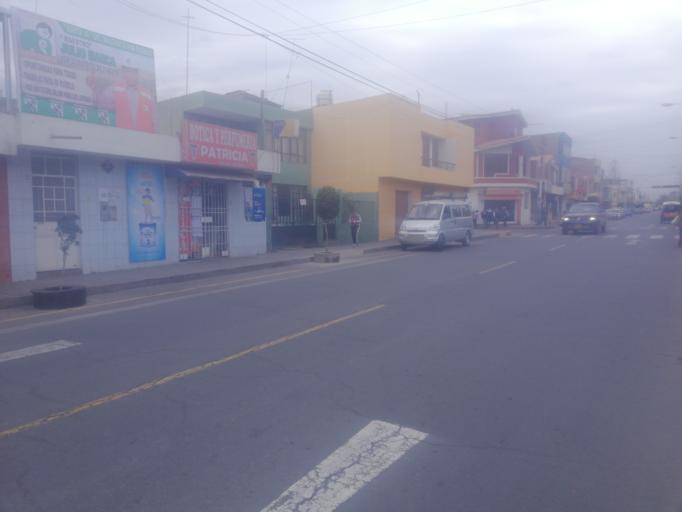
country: PE
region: Arequipa
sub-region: Provincia de Arequipa
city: Tiabaya
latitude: -16.4487
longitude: -71.5911
